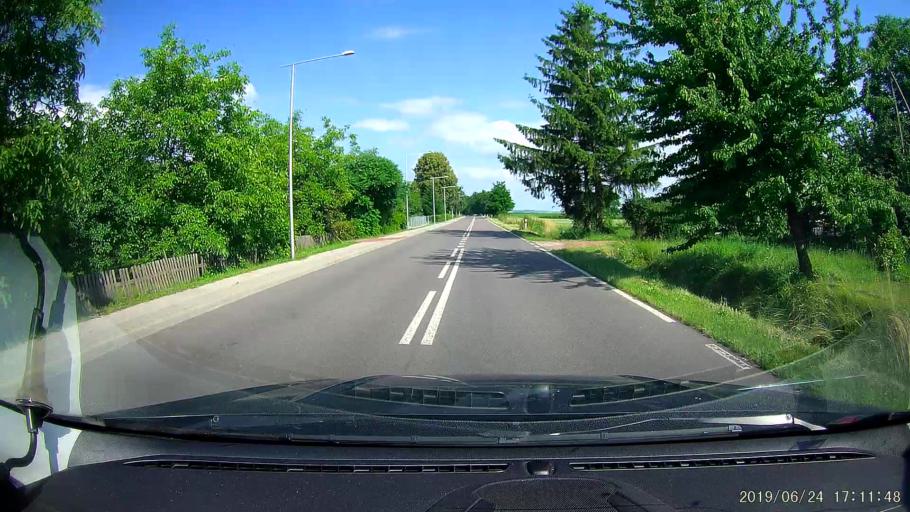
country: PL
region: Lublin Voivodeship
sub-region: Powiat hrubieszowski
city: Dolhobyczow
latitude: 50.5817
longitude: 24.0593
